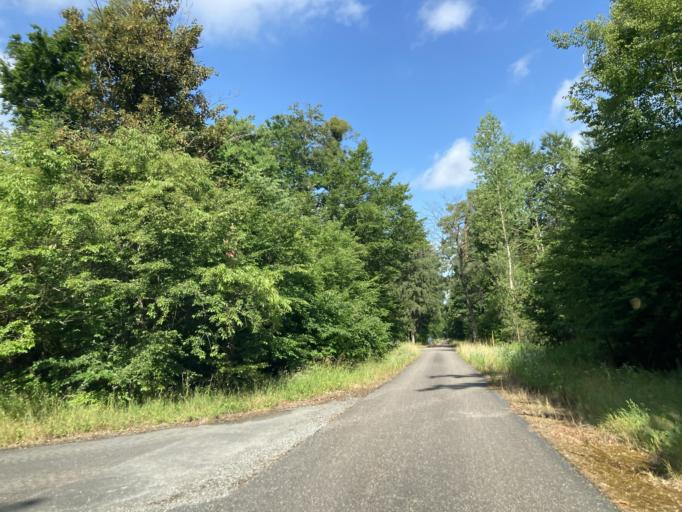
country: DE
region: Baden-Wuerttemberg
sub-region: Karlsruhe Region
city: Graben-Neudorf
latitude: 49.1598
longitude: 8.5179
